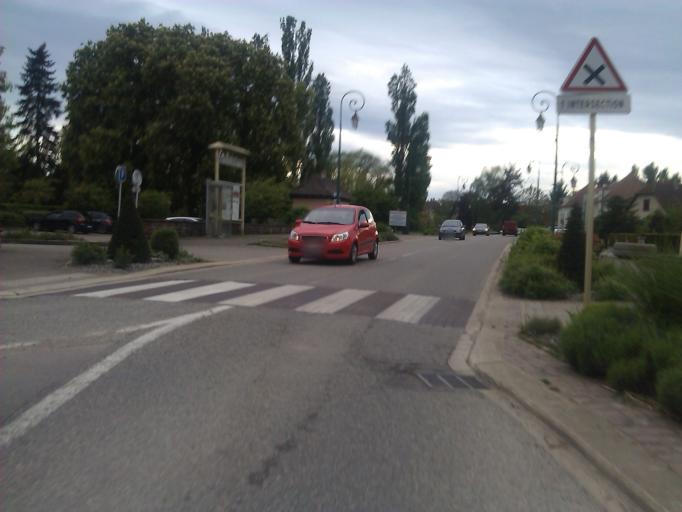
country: FR
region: Alsace
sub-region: Departement du Haut-Rhin
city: Guemar
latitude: 48.1886
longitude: 7.3953
